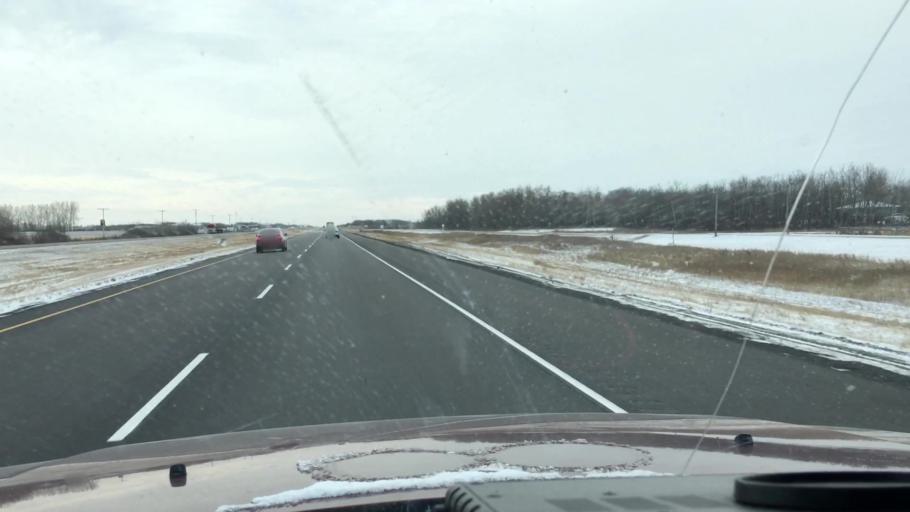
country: CA
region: Saskatchewan
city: Saskatoon
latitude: 51.9741
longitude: -106.5560
